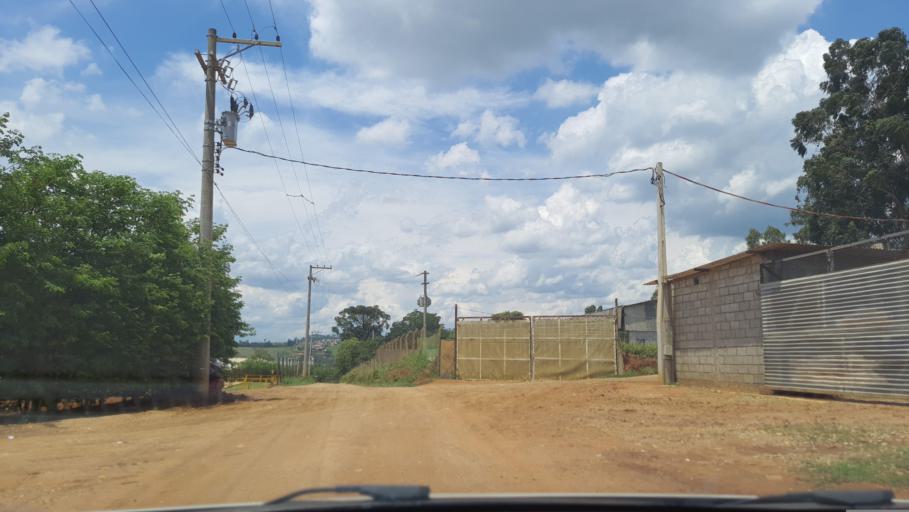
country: BR
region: Sao Paulo
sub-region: Bom Jesus Dos Perdoes
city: Bom Jesus dos Perdoes
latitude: -23.1510
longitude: -46.4615
